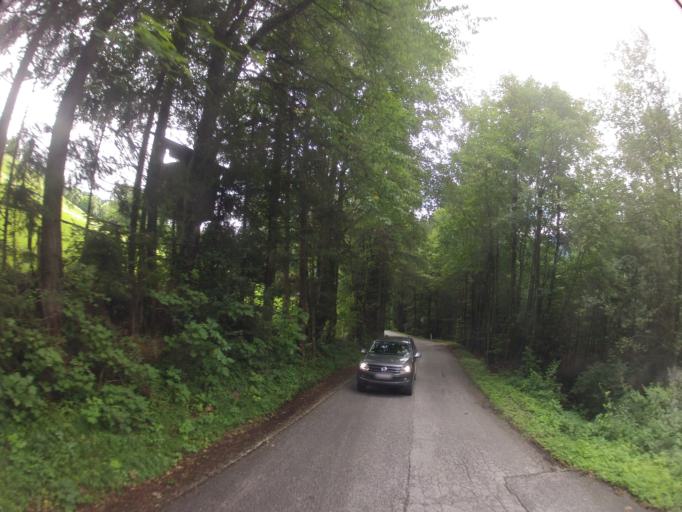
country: AT
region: Salzburg
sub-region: Politischer Bezirk Sankt Johann im Pongau
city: Werfen
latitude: 47.4895
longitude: 13.1969
